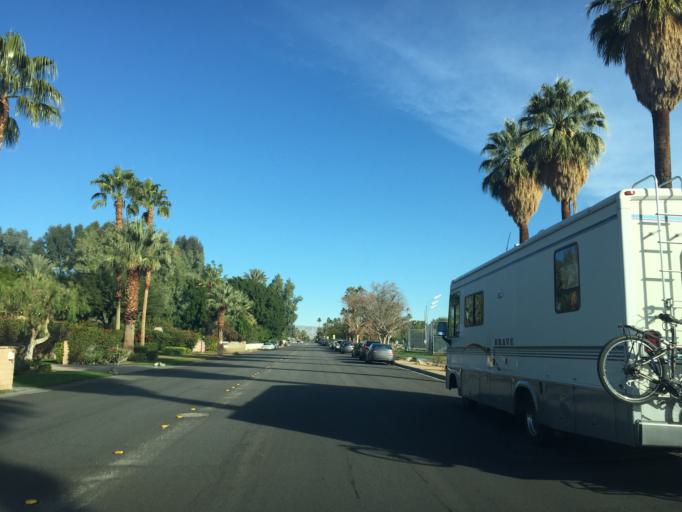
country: US
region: California
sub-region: Riverside County
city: Palm Springs
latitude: 33.8345
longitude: -116.5412
